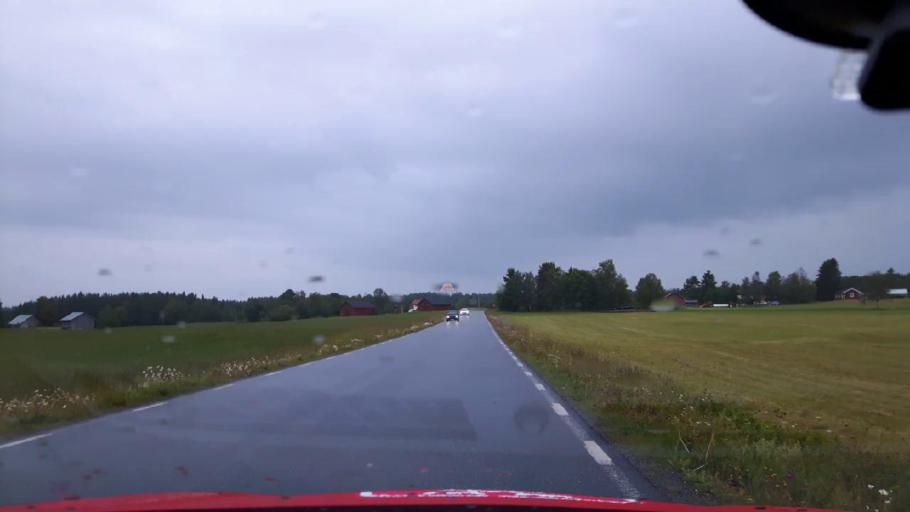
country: SE
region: Jaemtland
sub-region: OEstersunds Kommun
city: Brunflo
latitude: 63.0145
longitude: 14.7339
